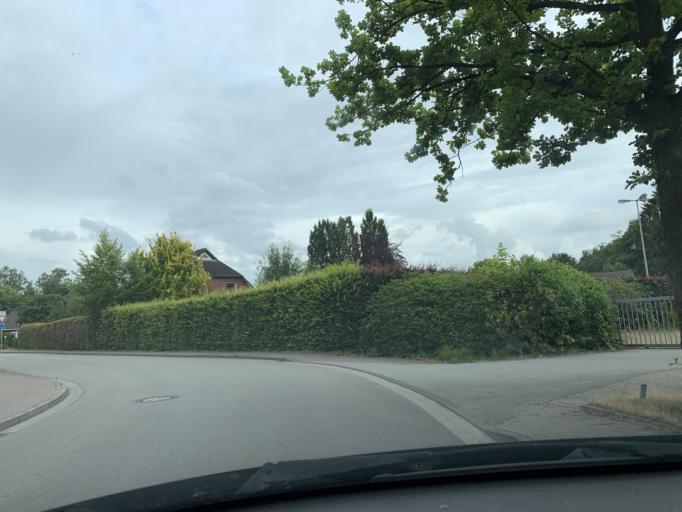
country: DE
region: Lower Saxony
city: Westerstede
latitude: 53.2538
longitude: 7.9167
